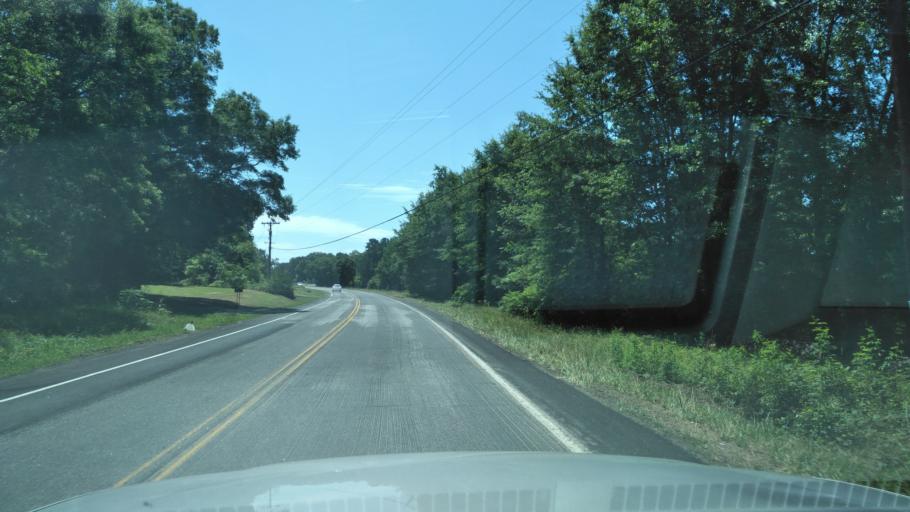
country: US
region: South Carolina
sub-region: Laurens County
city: Laurens
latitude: 34.5411
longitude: -82.0667
